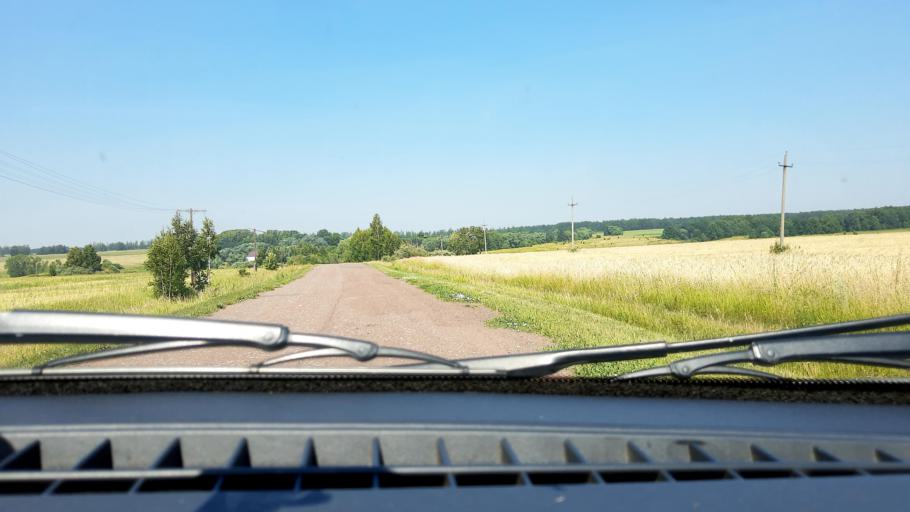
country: RU
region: Bashkortostan
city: Kushnarenkovo
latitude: 55.0632
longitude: 55.1636
